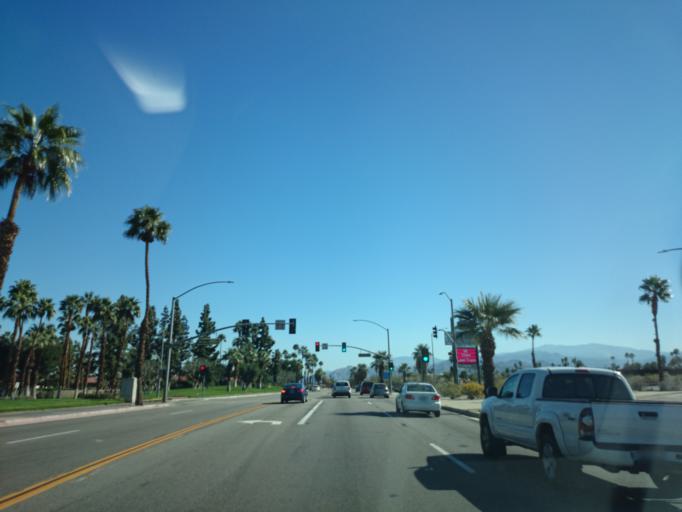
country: US
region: California
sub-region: Riverside County
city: Palm Springs
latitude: 33.8587
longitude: -116.5579
